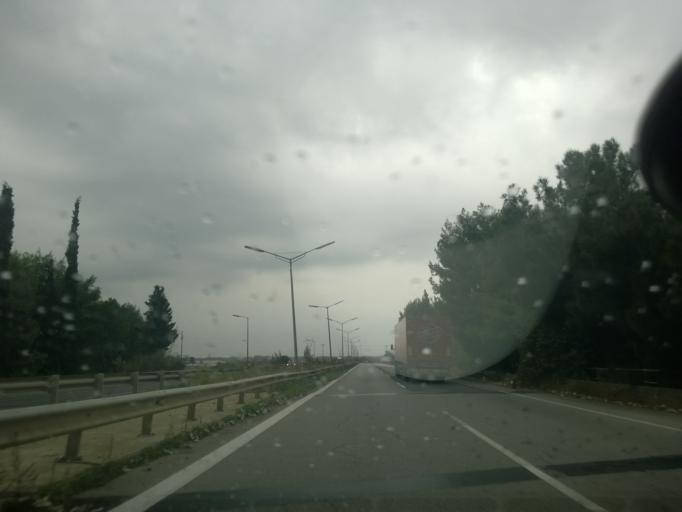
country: GR
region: Central Macedonia
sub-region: Nomos Thessalonikis
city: Agios Athanasios
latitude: 40.7230
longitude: 22.7143
